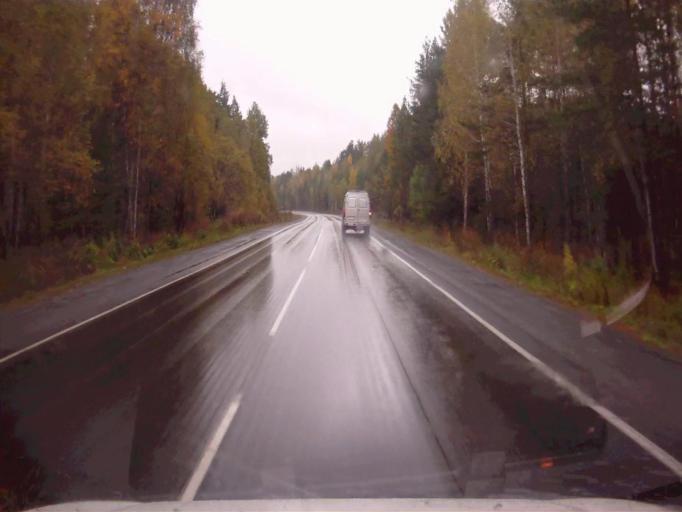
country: RU
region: Chelyabinsk
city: Tayginka
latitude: 55.5672
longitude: 60.6504
